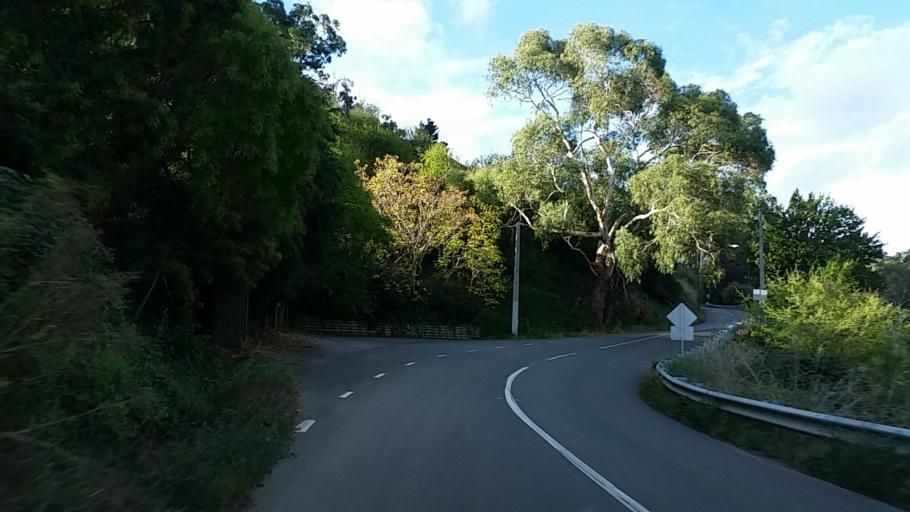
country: AU
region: South Australia
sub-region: Adelaide Hills
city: Adelaide Hills
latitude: -34.8905
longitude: 138.7395
